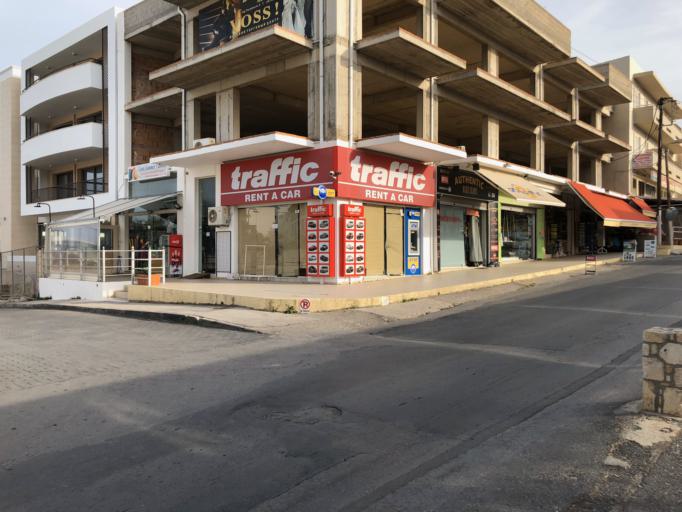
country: GR
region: Crete
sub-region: Nomos Irakleiou
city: Limin Khersonisou
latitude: 35.3227
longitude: 25.3877
